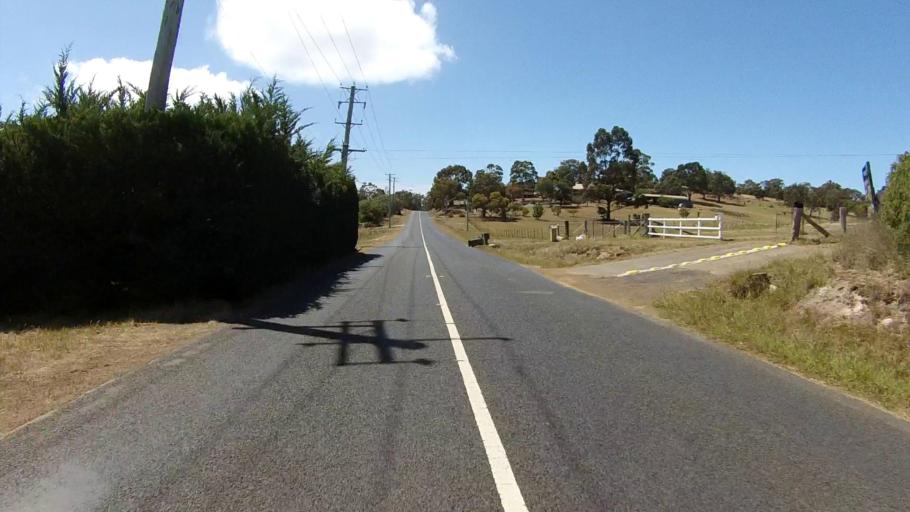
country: AU
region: Tasmania
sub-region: Clarence
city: Sandford
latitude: -42.9606
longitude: 147.4744
